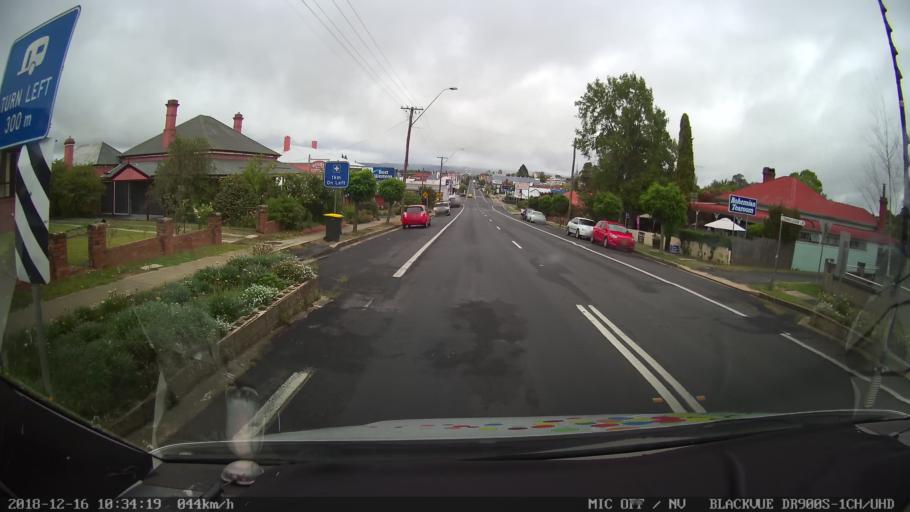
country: AU
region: New South Wales
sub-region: Tenterfield Municipality
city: Carrolls Creek
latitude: -29.0586
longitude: 152.0181
